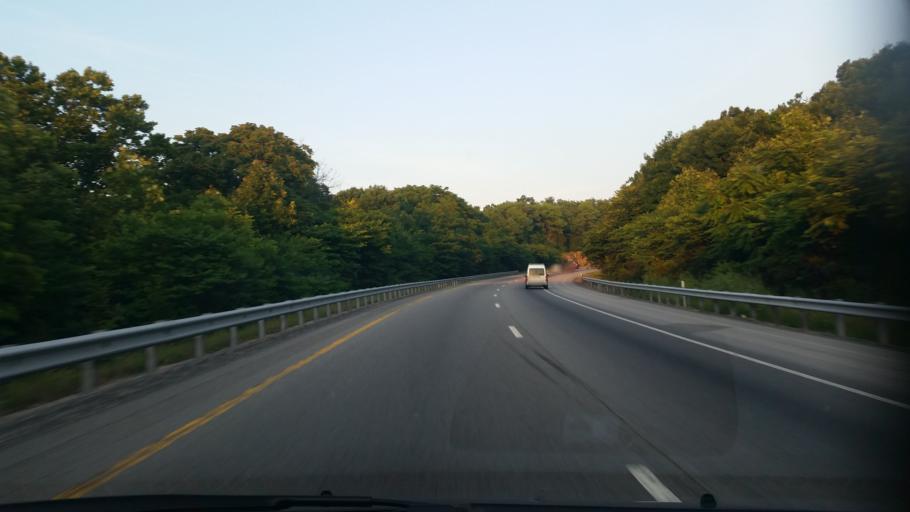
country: US
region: Tennessee
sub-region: Putnam County
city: Algood
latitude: 36.1440
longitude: -85.3708
